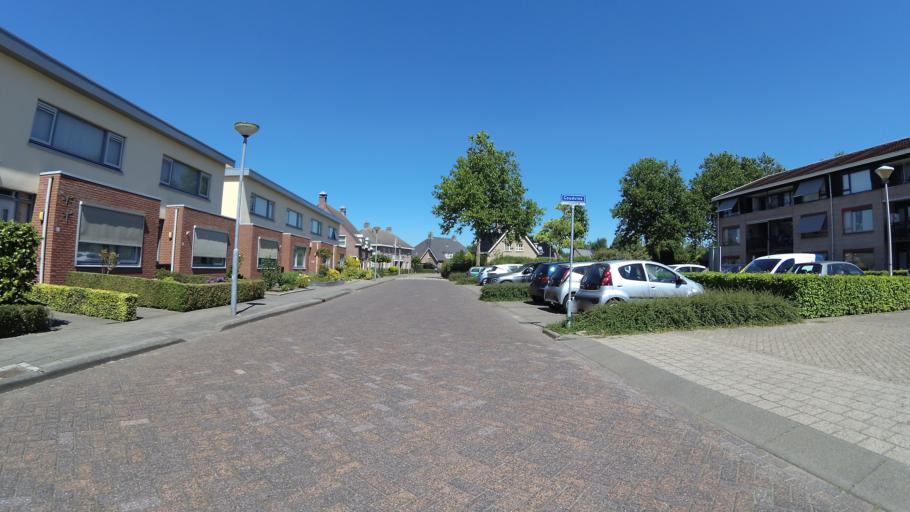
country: NL
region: North Brabant
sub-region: Gemeente Waalwijk
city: Waalwijk
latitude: 51.6746
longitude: 5.0152
